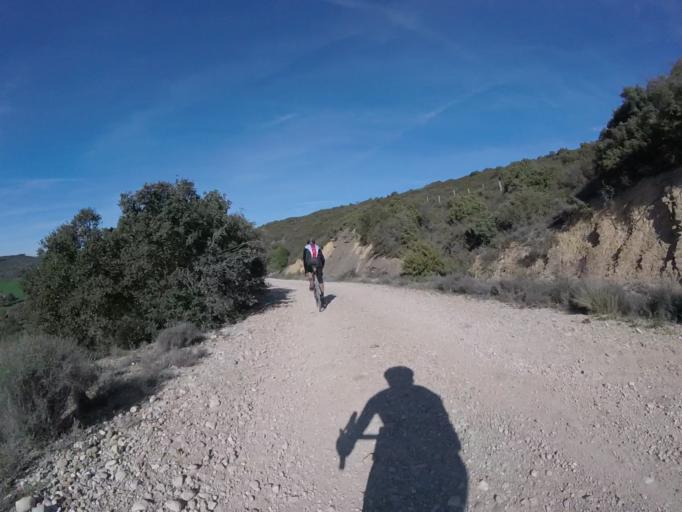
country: ES
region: Navarre
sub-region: Provincia de Navarra
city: Maneru
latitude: 42.6348
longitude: -1.8823
